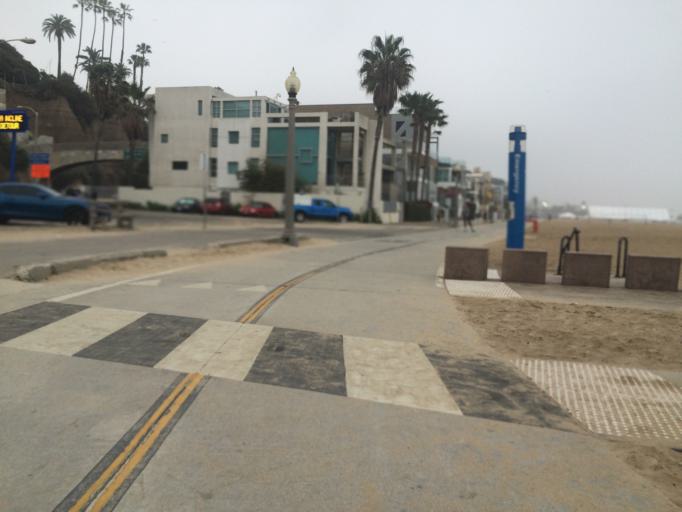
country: US
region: California
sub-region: Los Angeles County
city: Santa Monica
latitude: 34.0152
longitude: -118.5012
